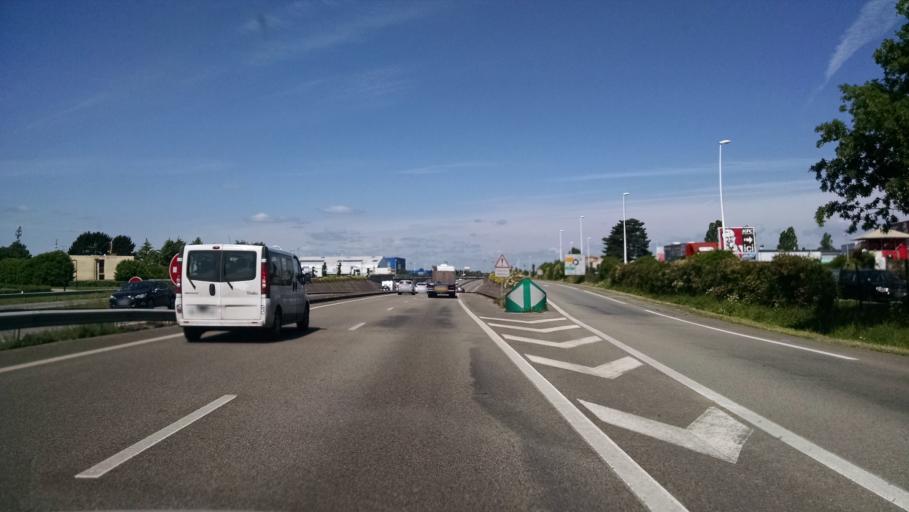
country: FR
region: Pays de la Loire
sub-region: Departement de la Loire-Atlantique
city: Saint-Herblain
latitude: 47.2273
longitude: -1.6322
